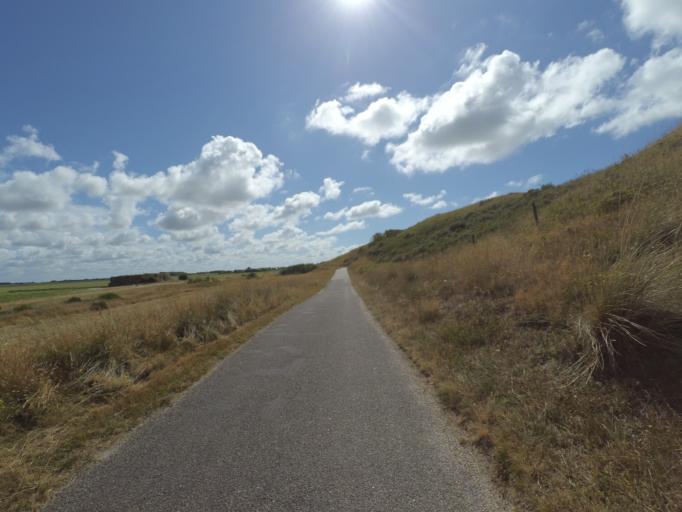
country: NL
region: North Holland
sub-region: Gemeente Texel
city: Den Burg
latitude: 53.1391
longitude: 4.8262
